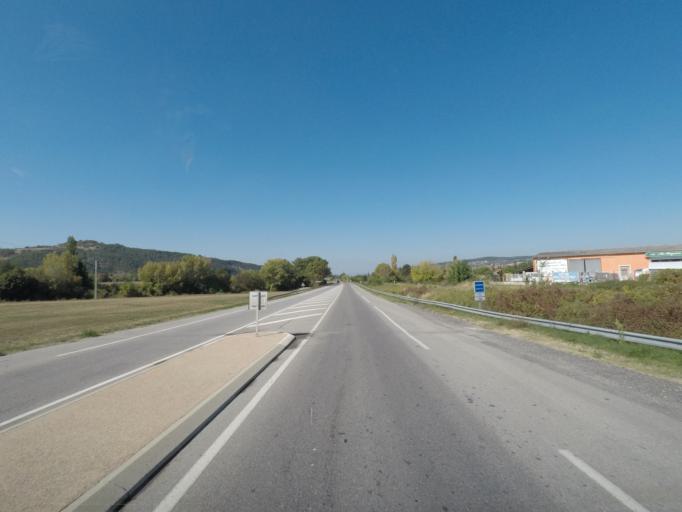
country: FR
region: Rhone-Alpes
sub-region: Departement de la Drome
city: Aouste-sur-Sye
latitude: 44.7104
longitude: 5.0576
